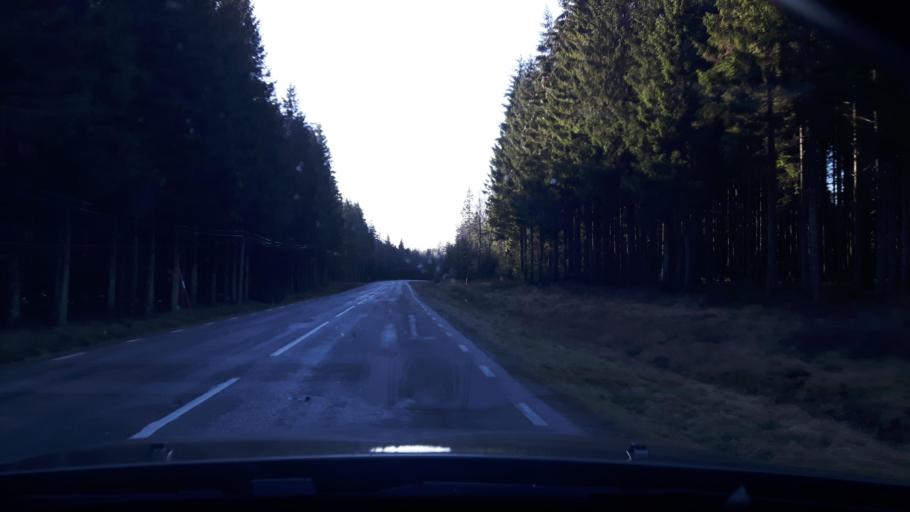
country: SE
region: Vaestra Goetaland
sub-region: Munkedals Kommun
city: Munkedal
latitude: 58.5515
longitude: 11.7190
